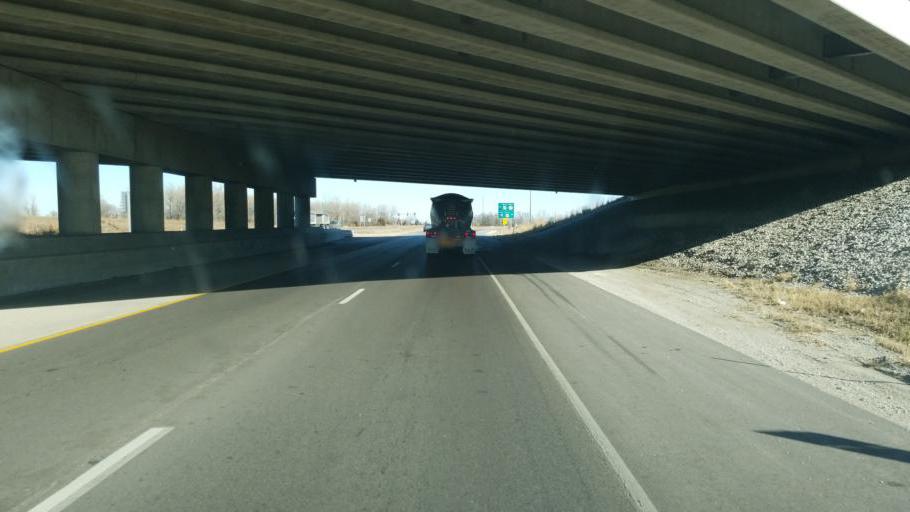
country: US
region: Iowa
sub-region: Polk County
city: Altoona
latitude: 41.6617
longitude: -93.4946
